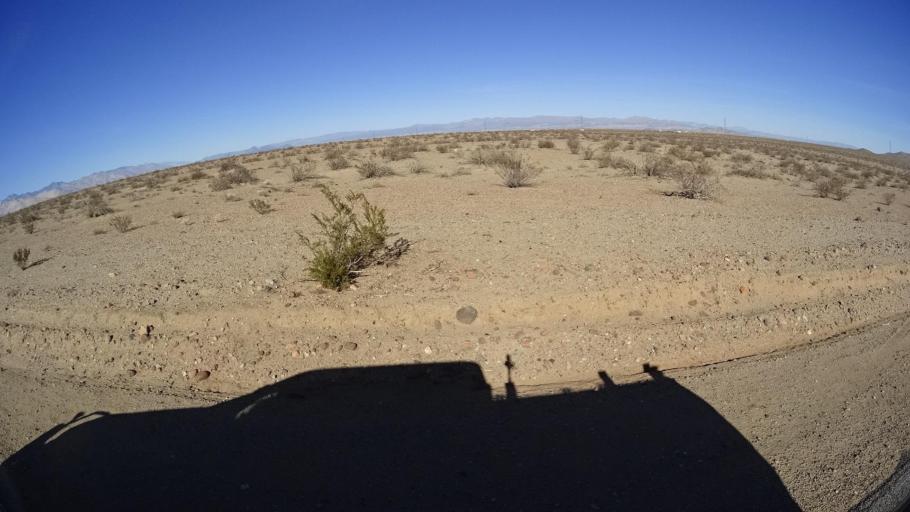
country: US
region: California
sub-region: Kern County
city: China Lake Acres
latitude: 35.5618
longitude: -117.7727
